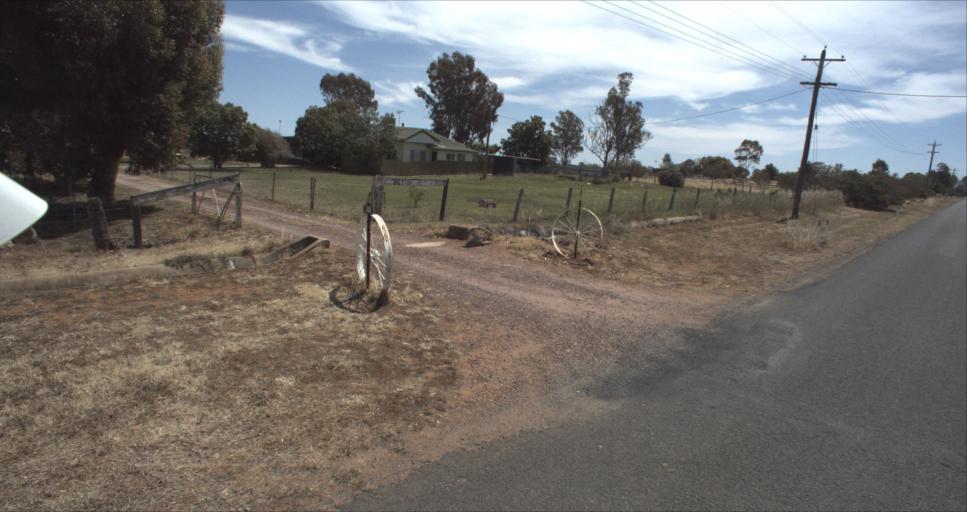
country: AU
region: New South Wales
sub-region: Leeton
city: Leeton
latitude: -34.5983
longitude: 146.4275
